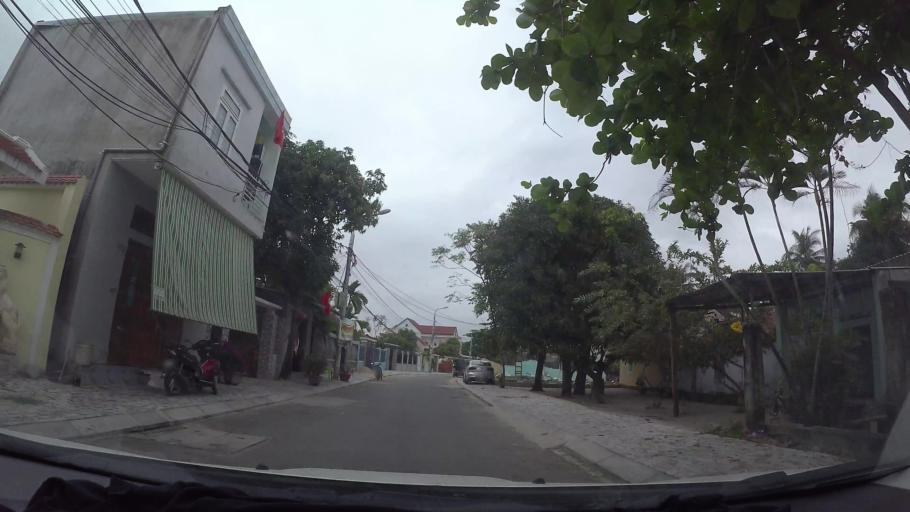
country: VN
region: Da Nang
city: Lien Chieu
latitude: 16.1053
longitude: 108.1297
